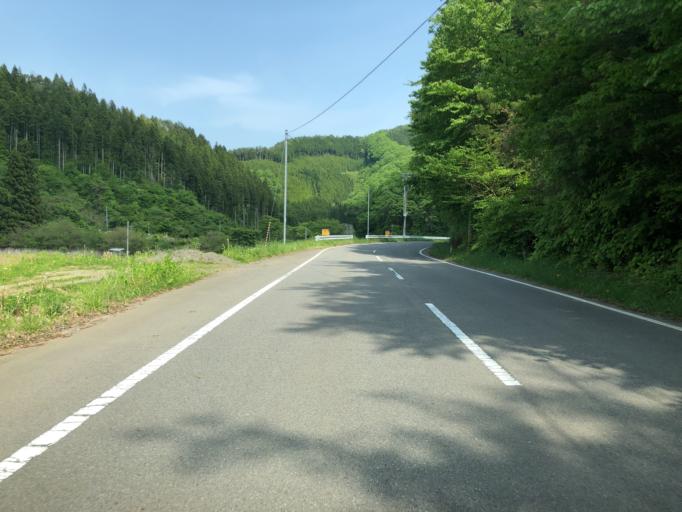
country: JP
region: Fukushima
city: Ishikawa
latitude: 36.9942
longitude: 140.6159
